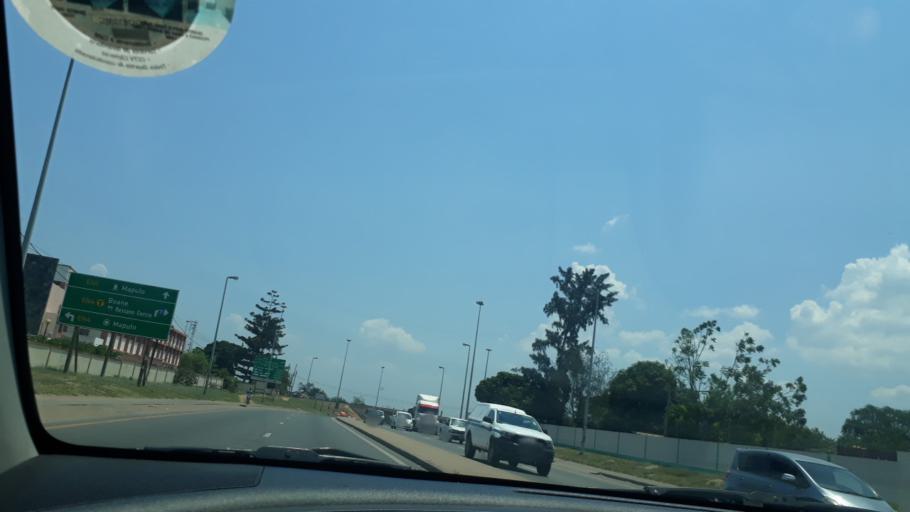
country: MZ
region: Maputo City
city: Maputo
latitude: -25.9409
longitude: 32.5447
